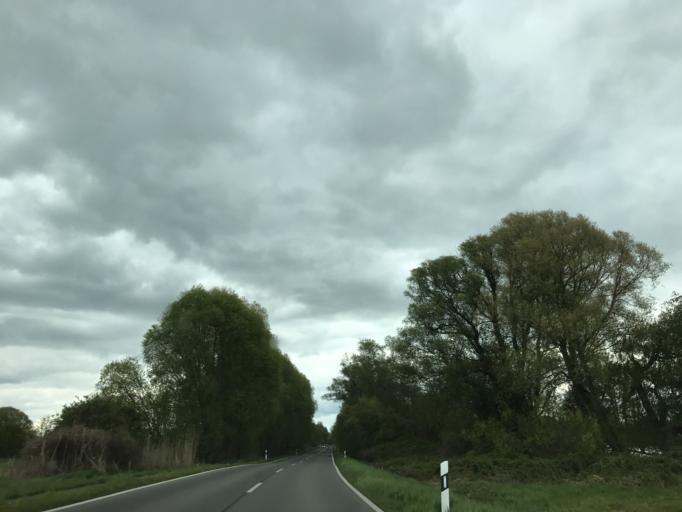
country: DE
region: Brandenburg
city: Ketzin
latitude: 52.4882
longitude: 12.7991
